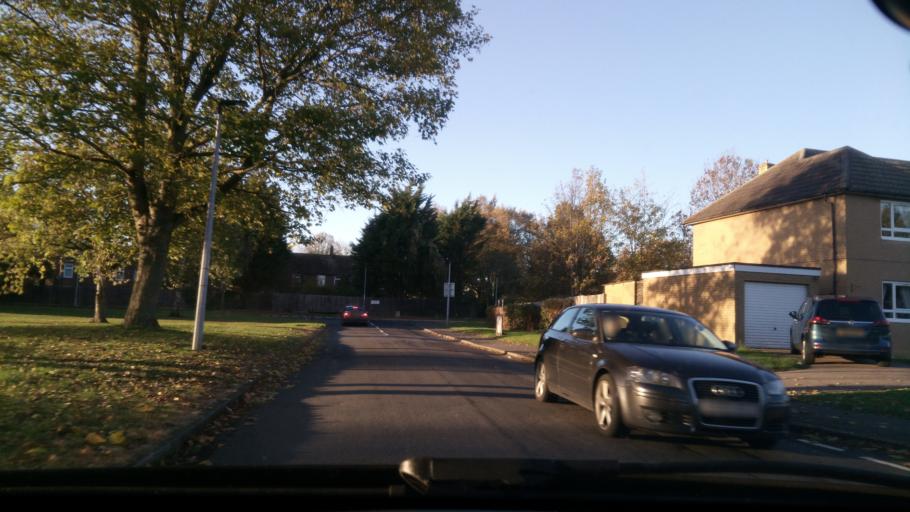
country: GB
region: England
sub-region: Peterborough
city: Wittering
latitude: 52.6108
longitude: -0.4418
